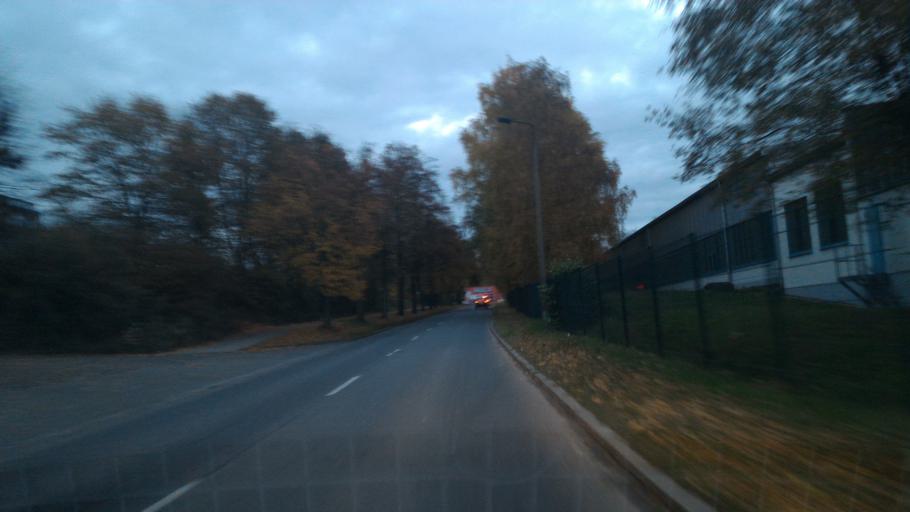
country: DE
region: Saxony
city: Neugersdorf
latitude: 50.9893
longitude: 14.6113
